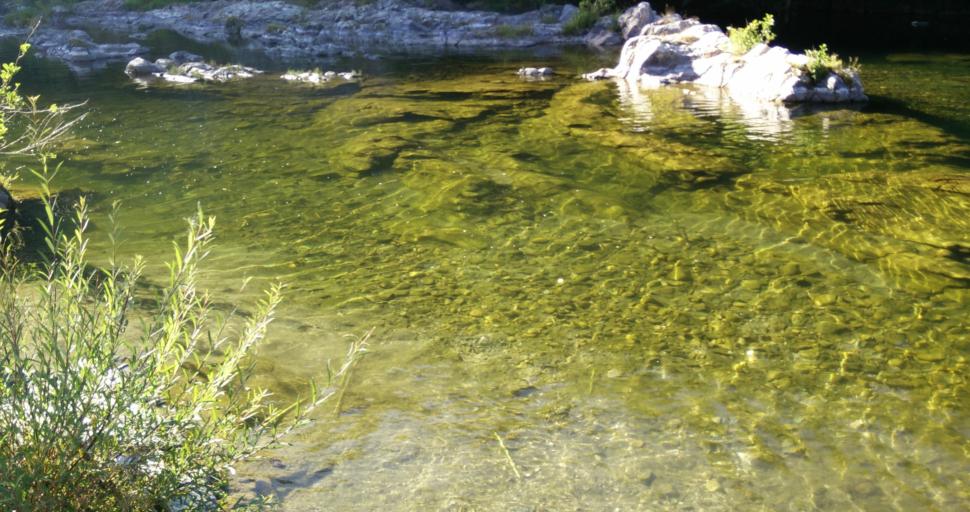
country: FR
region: Languedoc-Roussillon
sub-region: Departement du Gard
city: Saint-Jean-du-Gard
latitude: 44.1151
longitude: 3.8442
